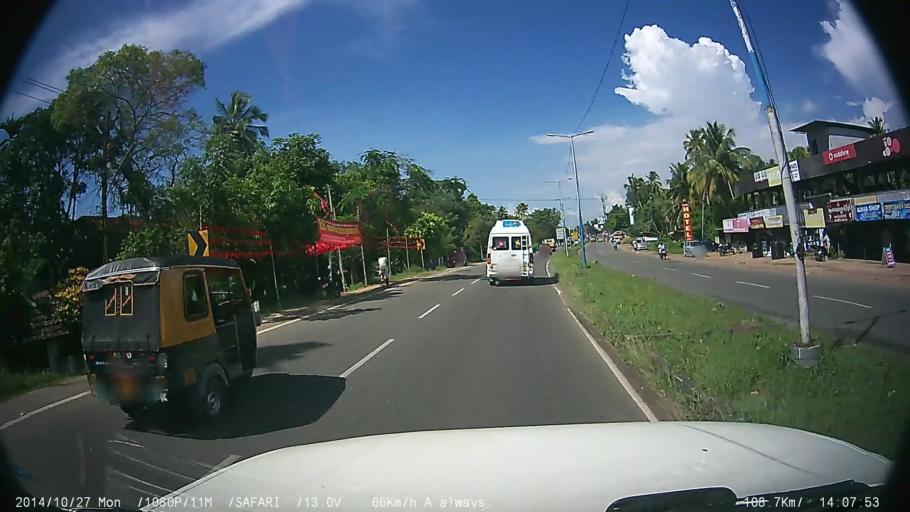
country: IN
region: Kerala
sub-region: Alappuzha
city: Kutiatodu
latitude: 9.7644
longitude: 76.3177
